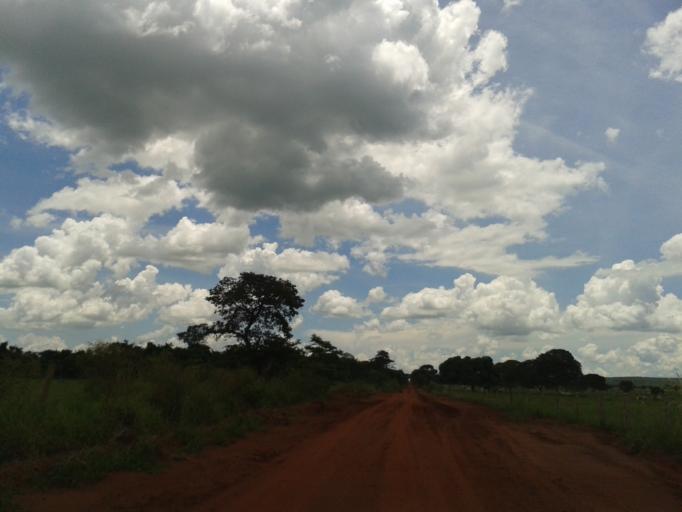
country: BR
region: Minas Gerais
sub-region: Ituiutaba
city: Ituiutaba
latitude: -18.8896
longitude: -49.4673
